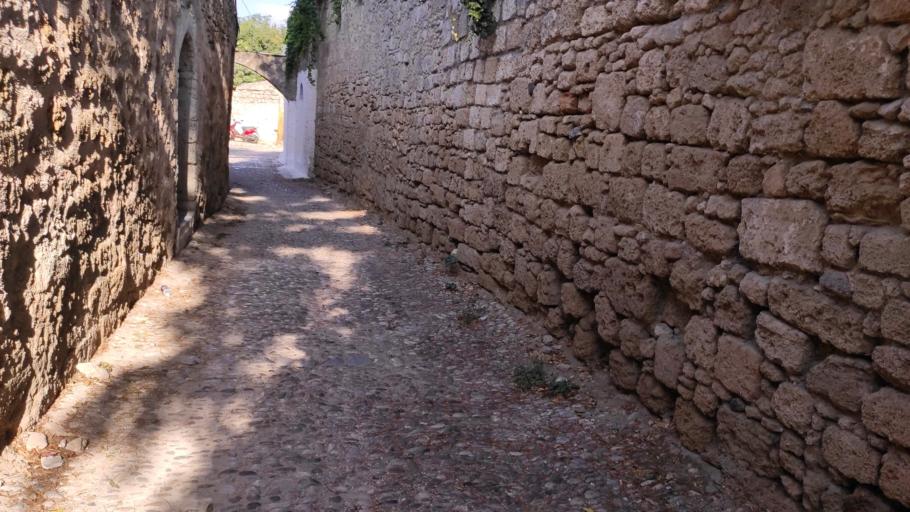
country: GR
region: South Aegean
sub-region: Nomos Dodekanisou
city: Rodos
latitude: 36.4431
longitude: 28.2237
